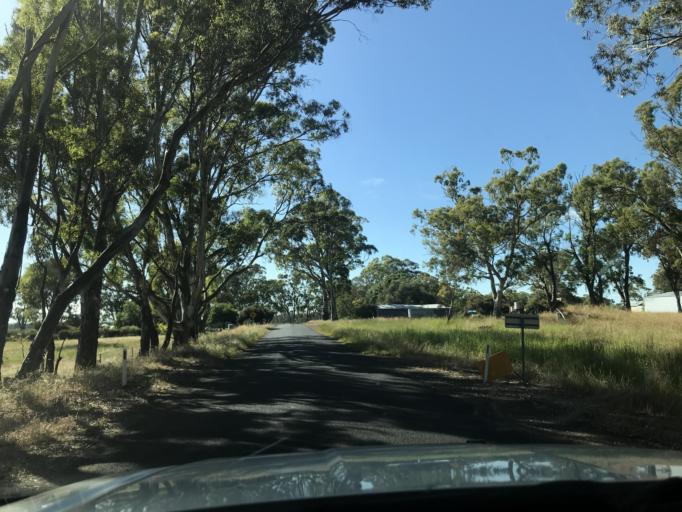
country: AU
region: Victoria
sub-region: Horsham
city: Horsham
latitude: -37.0319
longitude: 141.7278
